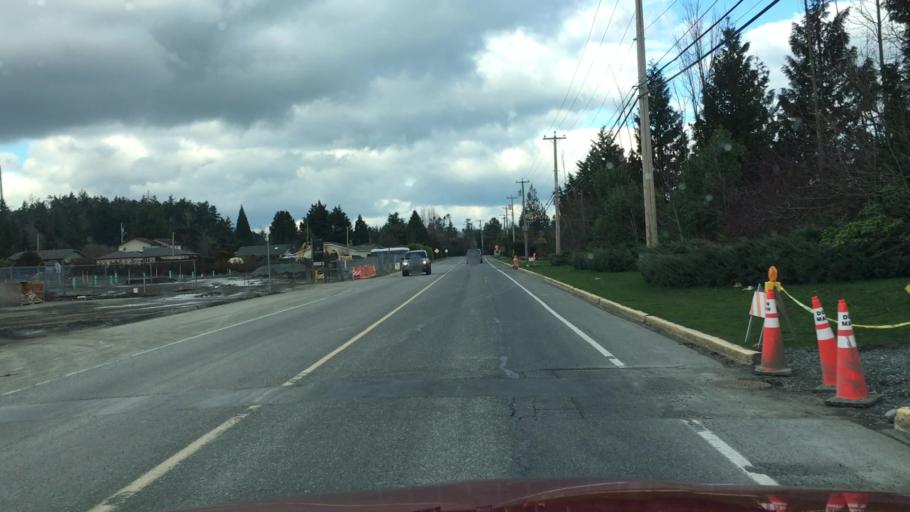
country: CA
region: British Columbia
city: North Saanich
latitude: 48.5968
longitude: -123.3946
